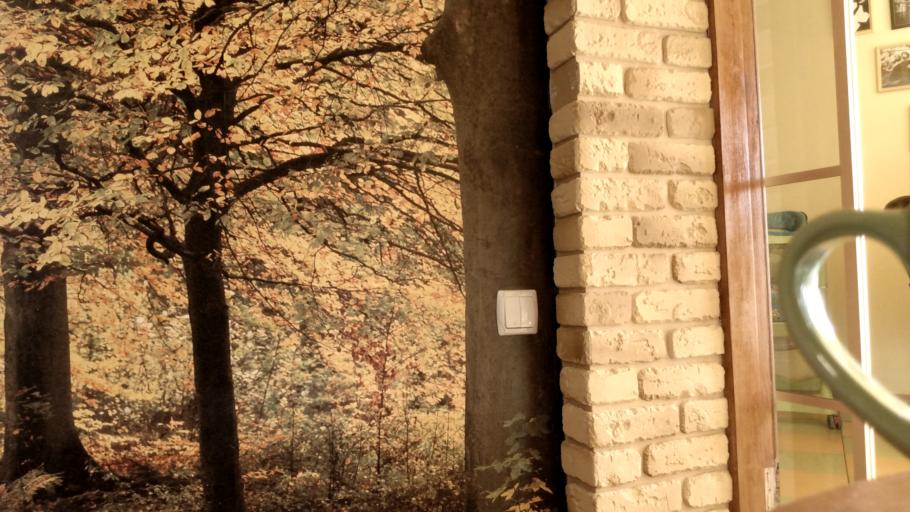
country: RU
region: Vologda
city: Imeni Zhelyabova
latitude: 58.8040
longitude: 36.8892
